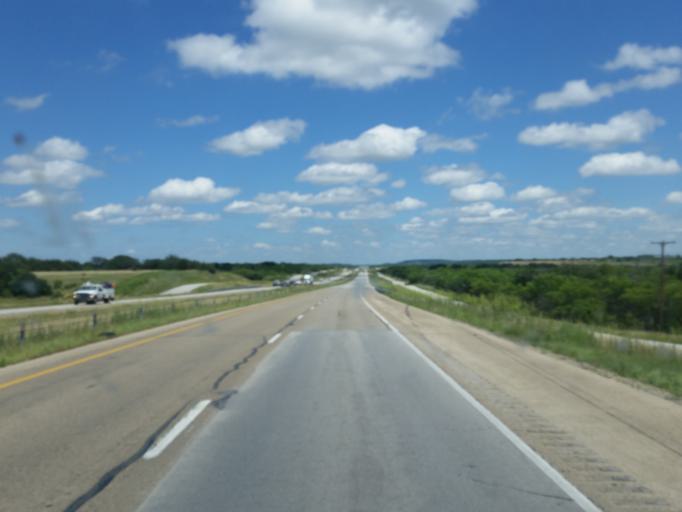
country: US
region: Texas
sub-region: Callahan County
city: Baird
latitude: 32.3849
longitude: -99.2911
